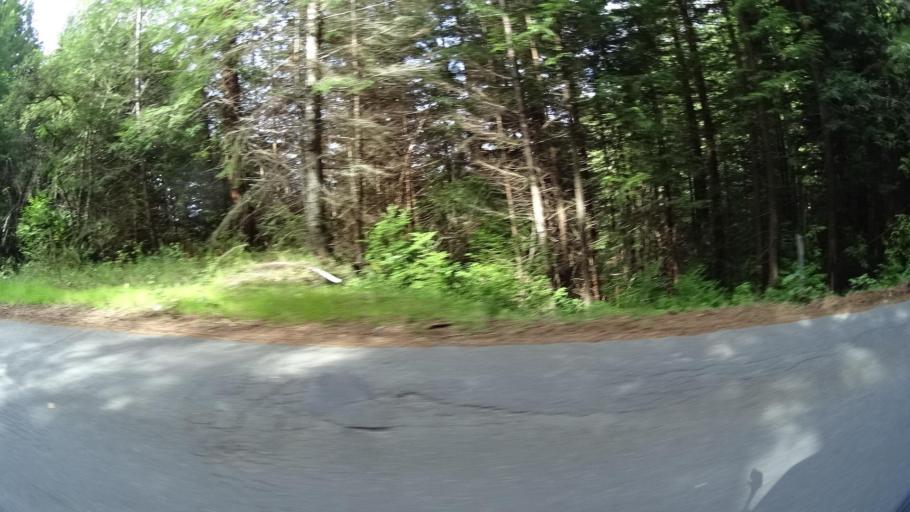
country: US
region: California
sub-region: Humboldt County
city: Bayside
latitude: 40.7557
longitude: -124.0379
